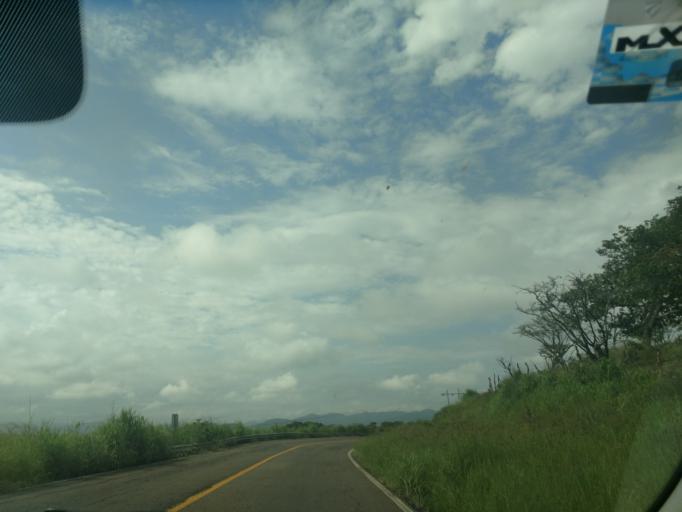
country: MX
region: Jalisco
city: El Salto
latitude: 20.3889
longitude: -104.5286
